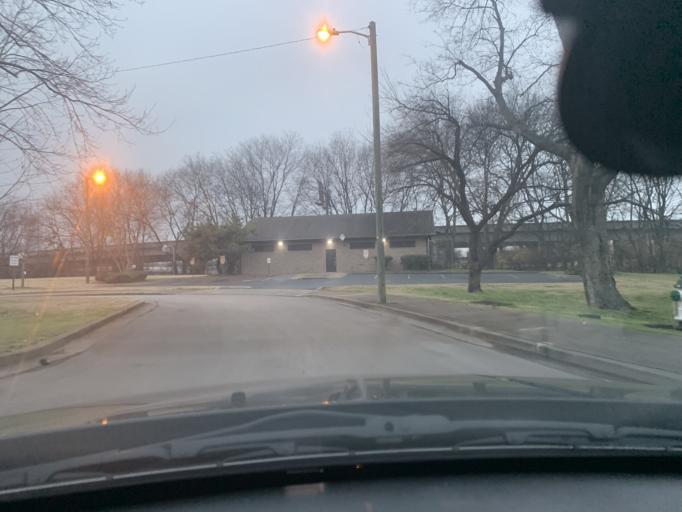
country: US
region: Tennessee
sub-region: Davidson County
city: Nashville
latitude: 36.1757
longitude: -86.7647
